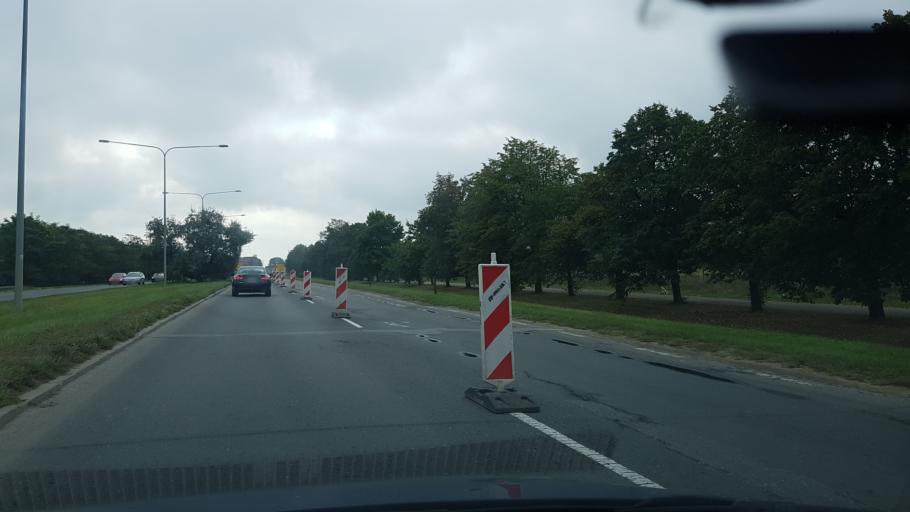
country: PL
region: Masovian Voivodeship
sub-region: Warszawa
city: Wilanow
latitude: 52.1579
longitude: 21.0882
